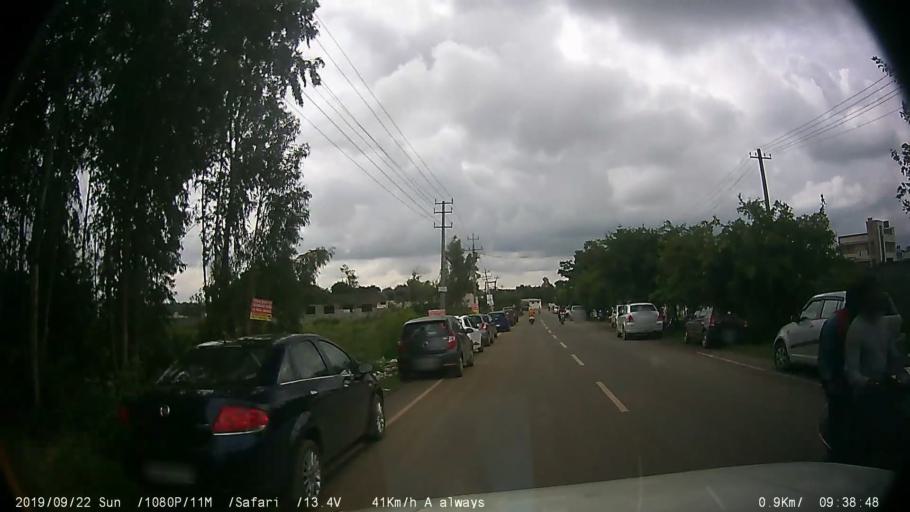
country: IN
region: Karnataka
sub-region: Bangalore Urban
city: Anekal
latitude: 12.8190
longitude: 77.6265
